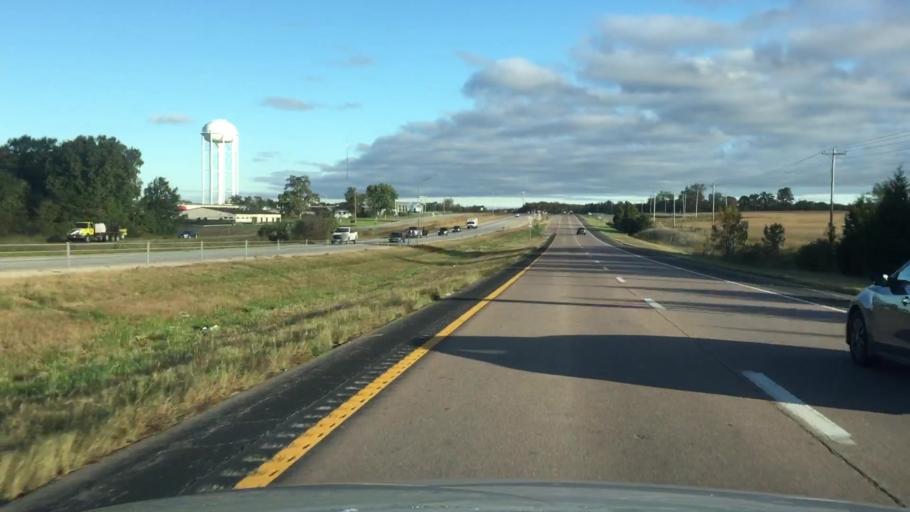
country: US
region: Missouri
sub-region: Boone County
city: Ashland
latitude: 38.8657
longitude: -92.2506
